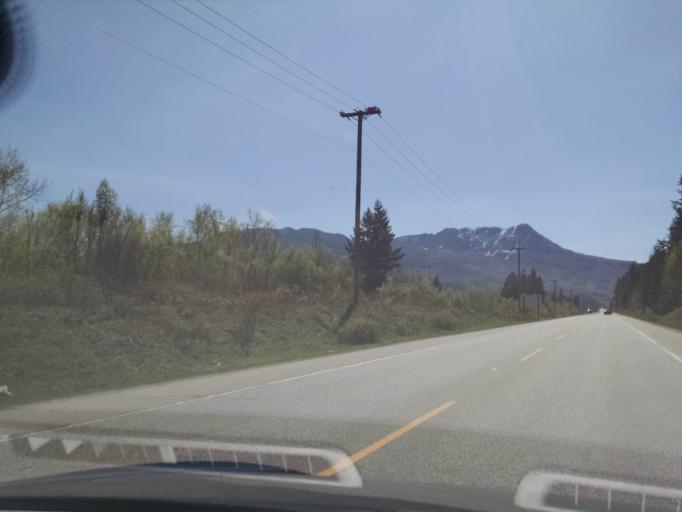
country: CA
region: British Columbia
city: Salmon Arm
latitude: 50.7251
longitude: -119.3166
